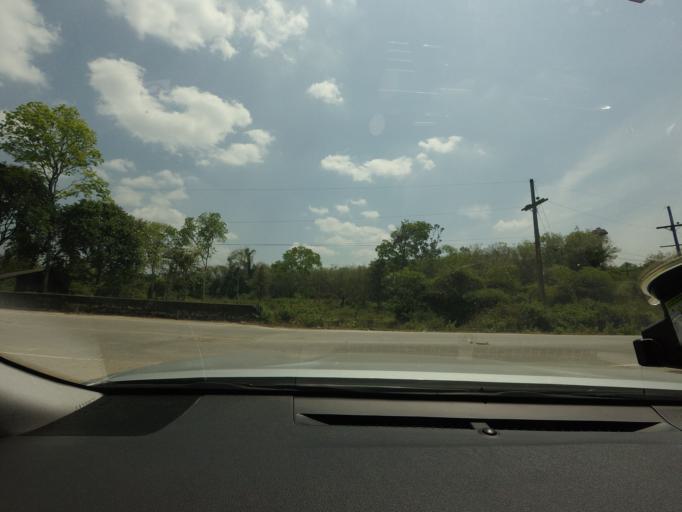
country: TH
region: Narathiwat
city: Rueso
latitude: 6.3901
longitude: 101.5023
